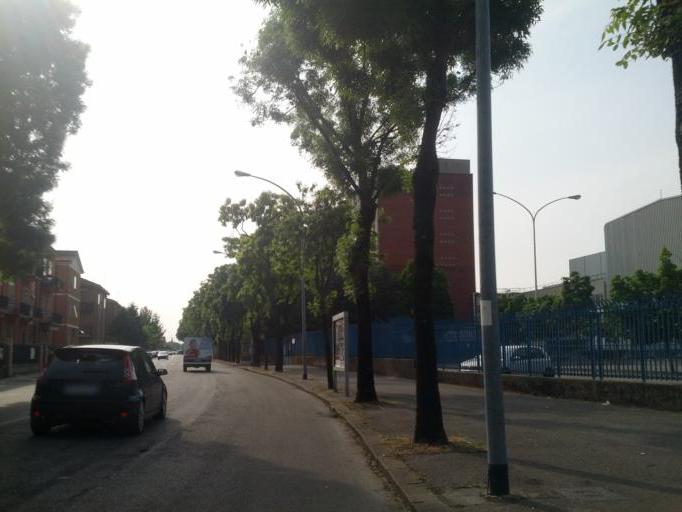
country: IT
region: Veneto
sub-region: Provincia di Verona
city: Montorio
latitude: 45.4388
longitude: 11.0398
